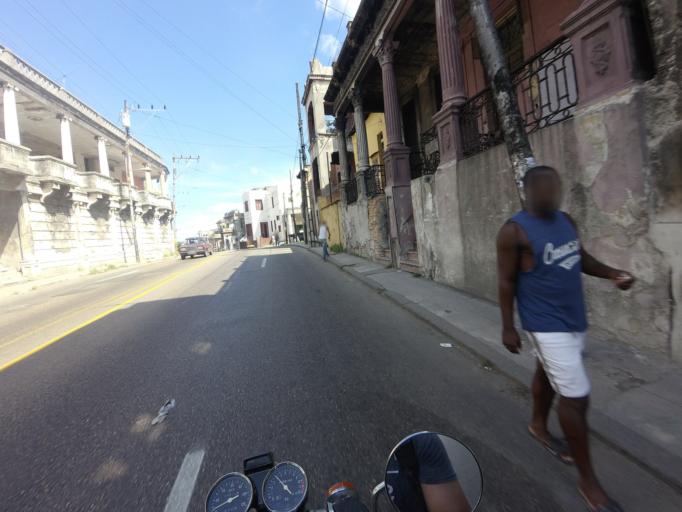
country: CU
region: La Habana
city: Diez de Octubre
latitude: 23.0986
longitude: -82.3621
